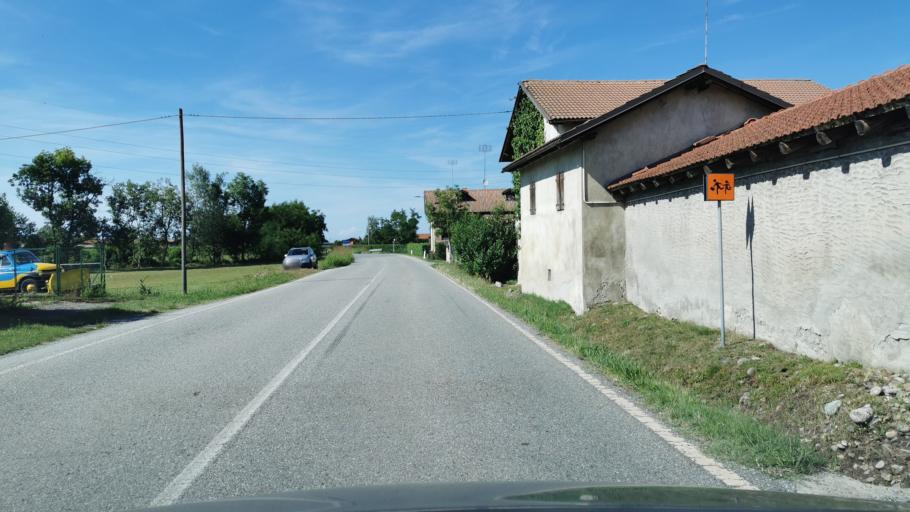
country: IT
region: Piedmont
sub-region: Provincia di Cuneo
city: Boves
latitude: 44.3570
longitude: 7.5599
